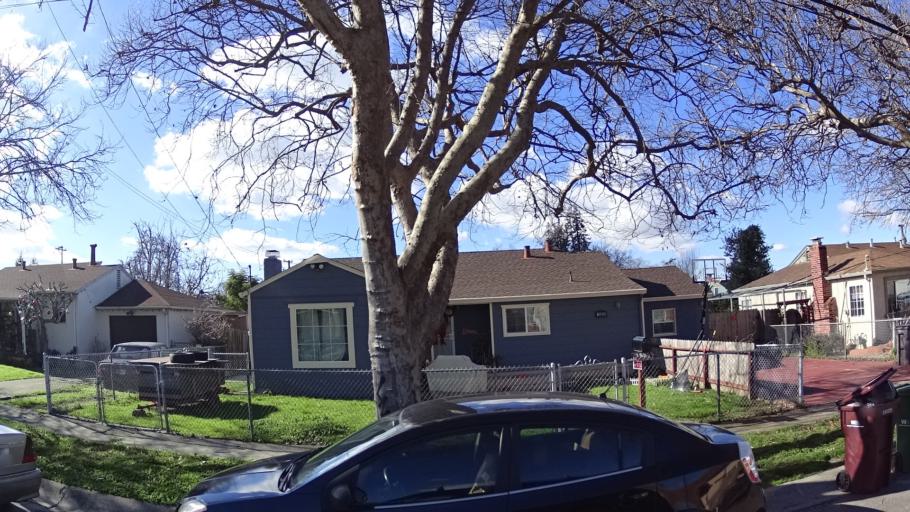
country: US
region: California
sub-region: Alameda County
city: Ashland
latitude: 37.6874
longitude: -122.1143
